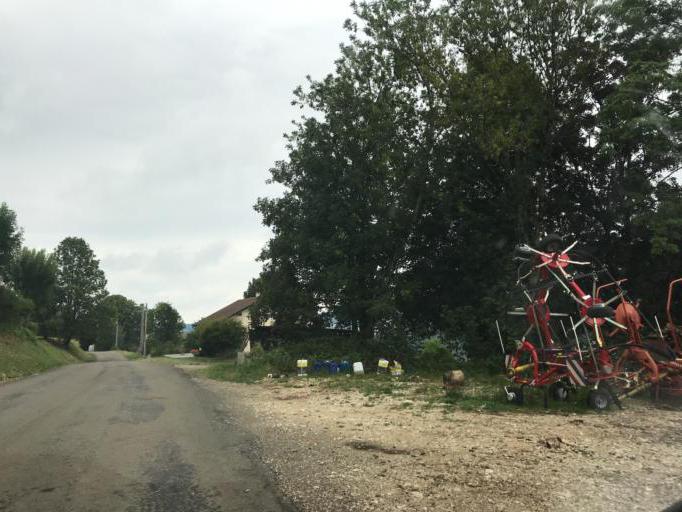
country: FR
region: Franche-Comte
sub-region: Departement du Jura
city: Lavans-les-Saint-Claude
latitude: 46.3234
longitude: 5.7456
